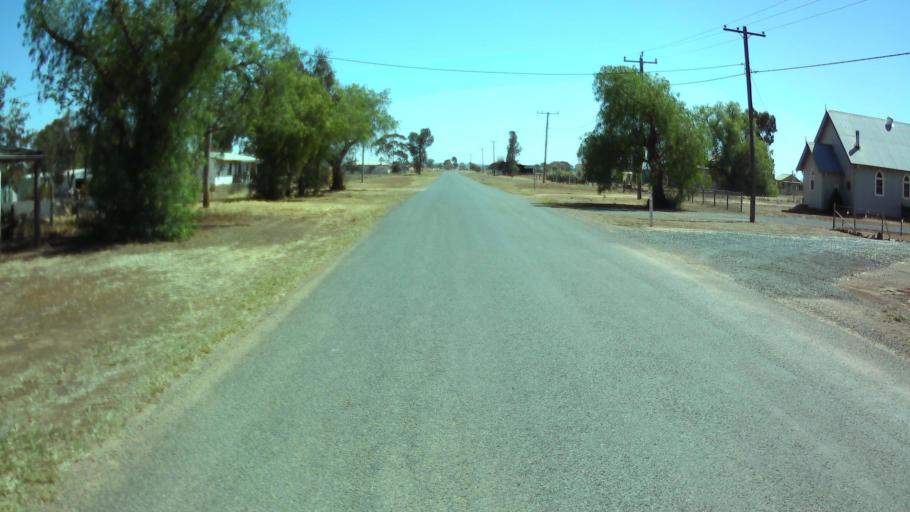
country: AU
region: New South Wales
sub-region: Weddin
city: Grenfell
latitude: -33.8431
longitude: 147.7440
